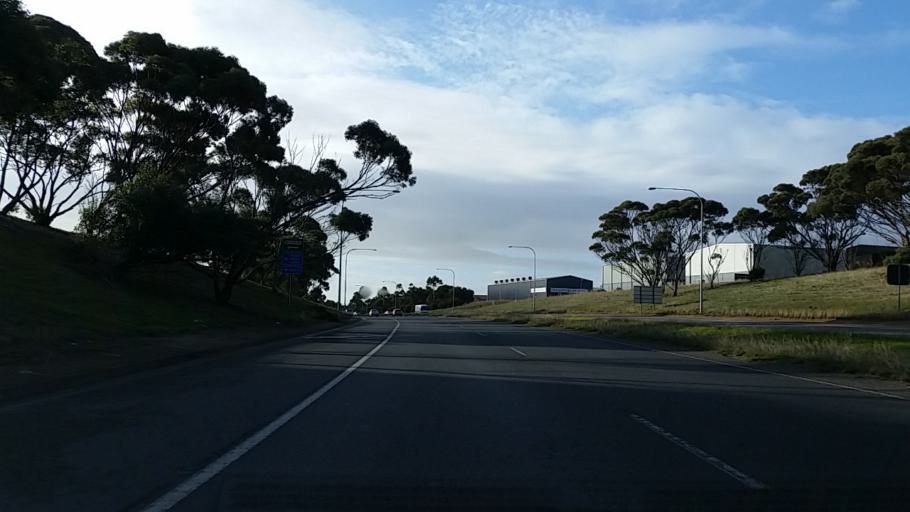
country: AU
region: South Australia
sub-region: Onkaparinga
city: Reynella
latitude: -35.1047
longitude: 138.4997
